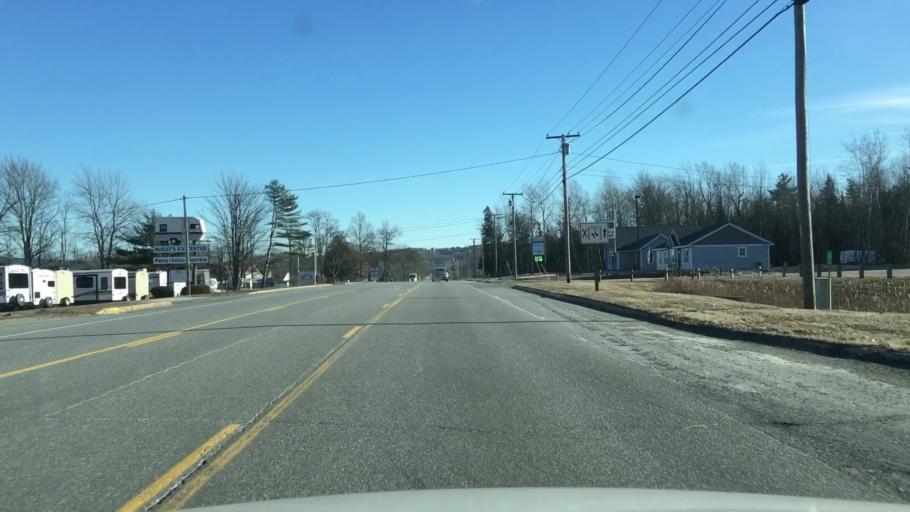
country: US
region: Maine
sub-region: Penobscot County
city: Holden
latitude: 44.7644
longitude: -68.7054
